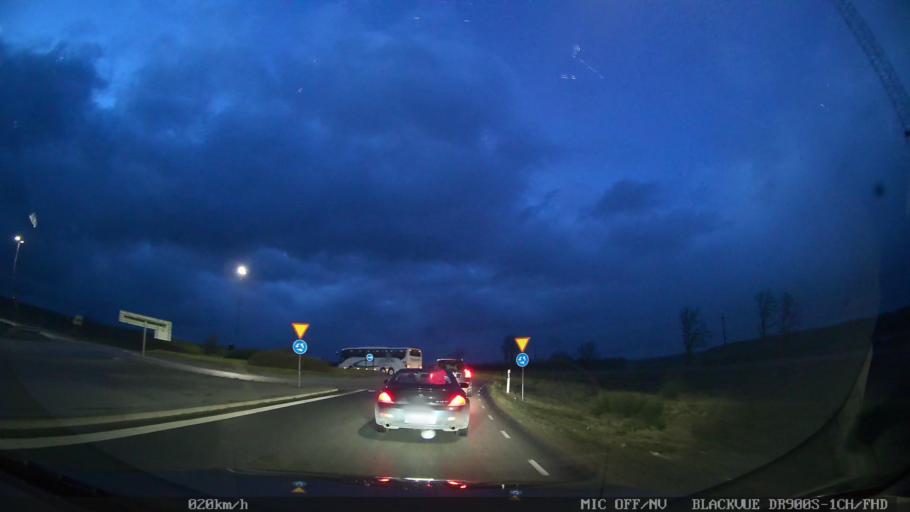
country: SE
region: Skane
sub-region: Hassleholms Kommun
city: Hassleholm
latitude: 56.1817
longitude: 13.7551
